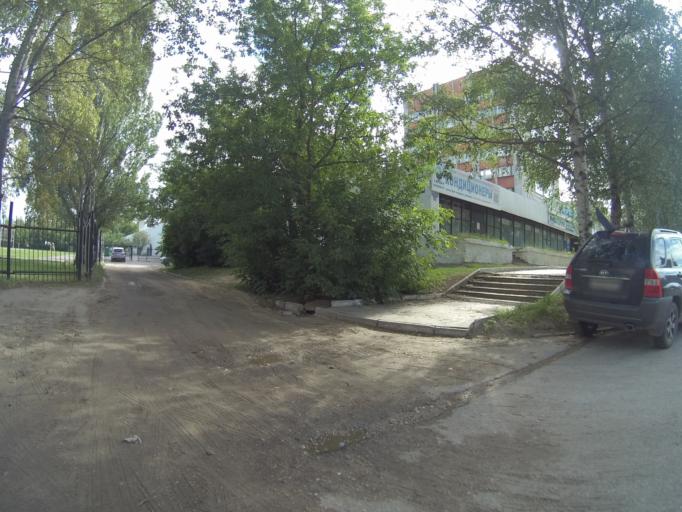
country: RU
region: Vladimir
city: Vladimir
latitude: 56.1506
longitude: 40.4342
